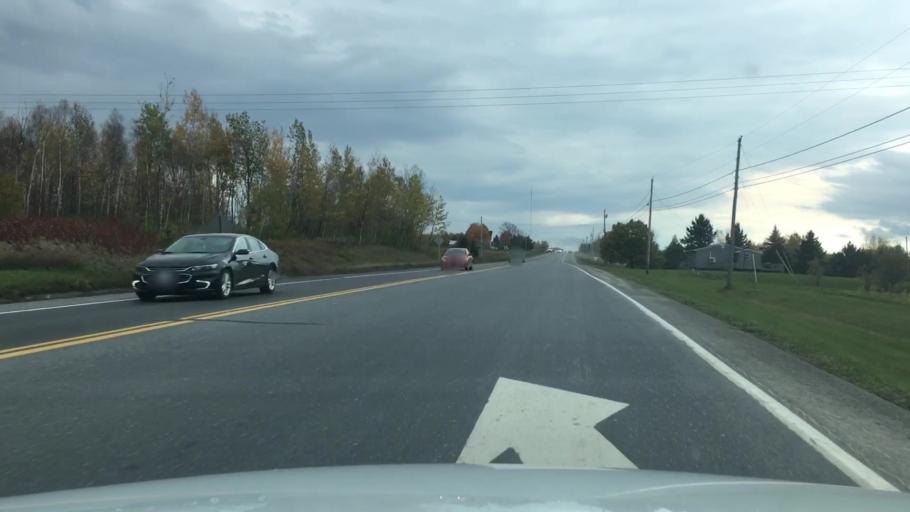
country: US
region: Maine
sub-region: Aroostook County
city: Caribou
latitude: 46.7787
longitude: -67.9892
